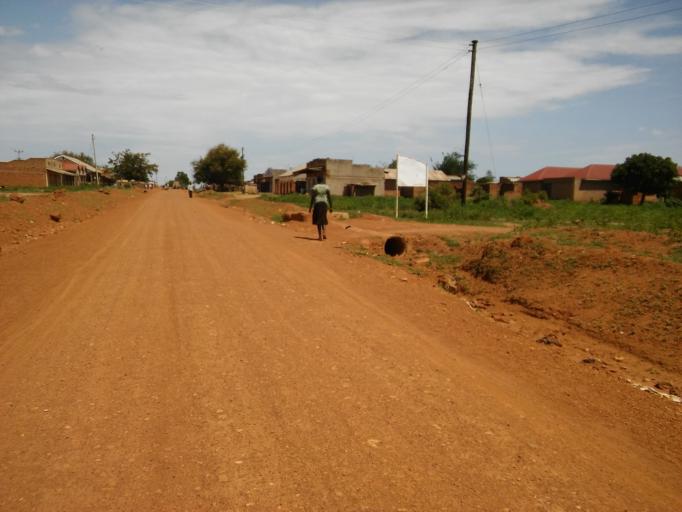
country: UG
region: Eastern Region
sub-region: Kumi District
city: Kumi
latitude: 1.4721
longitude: 33.8687
